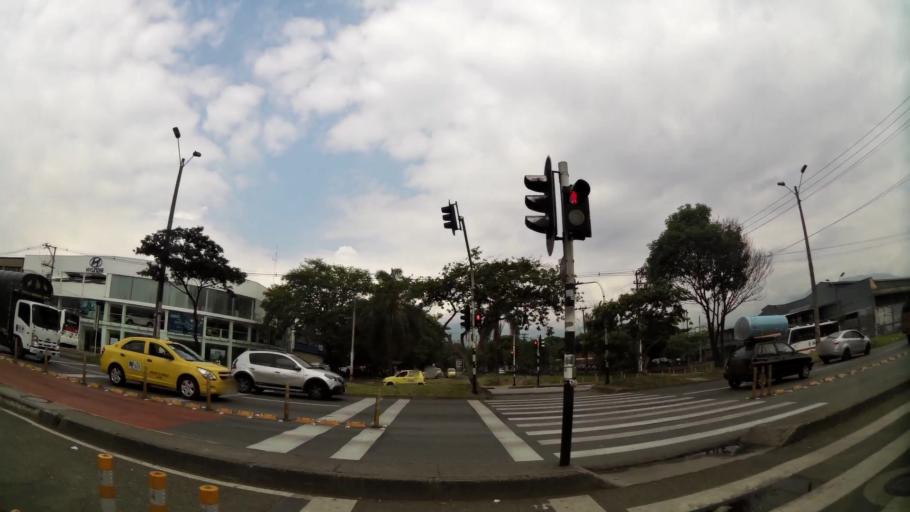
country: CO
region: Antioquia
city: Itagui
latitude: 6.2175
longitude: -75.5807
